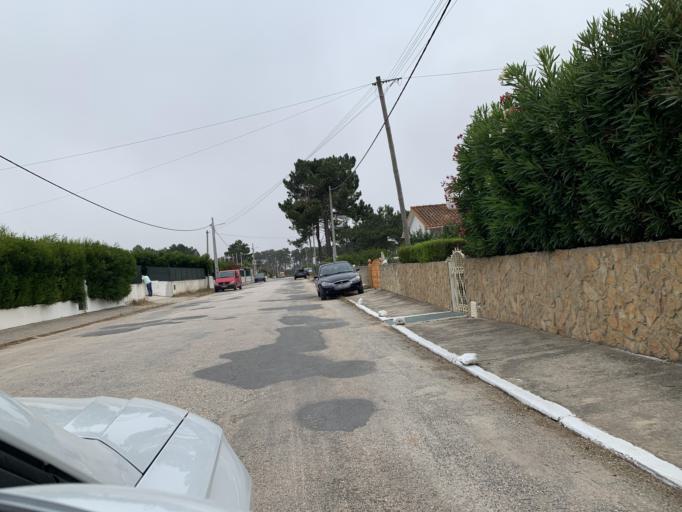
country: PT
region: Faro
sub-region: Aljezur
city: Aljezur
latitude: 37.3071
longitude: -8.8521
